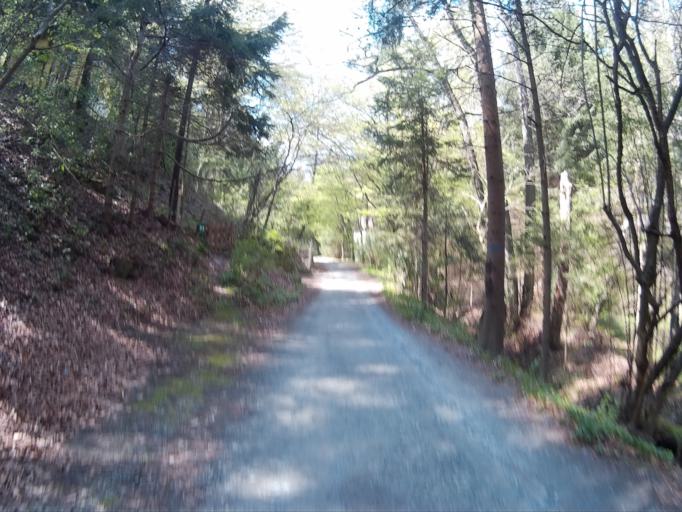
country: AT
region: Burgenland
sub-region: Politischer Bezirk Oberwart
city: Rechnitz
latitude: 47.3468
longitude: 16.4837
